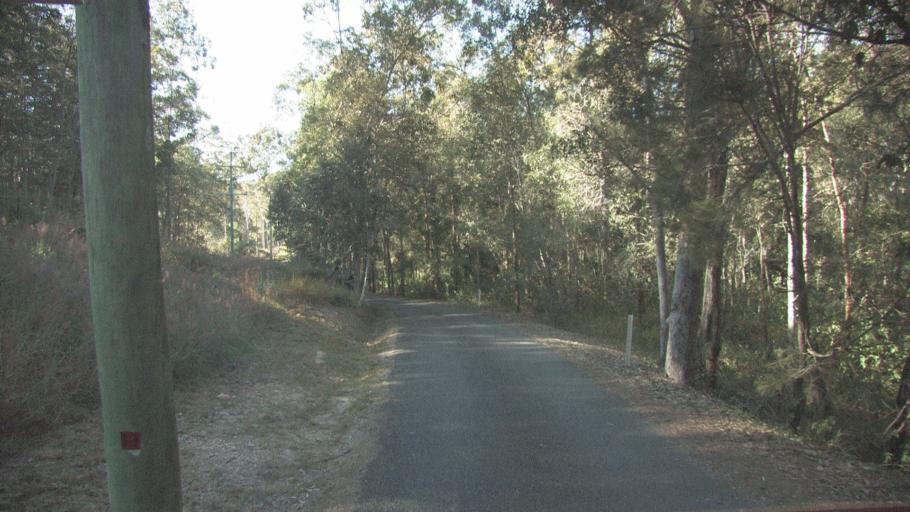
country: AU
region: Queensland
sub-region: Logan
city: Windaroo
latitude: -27.7936
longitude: 153.1705
